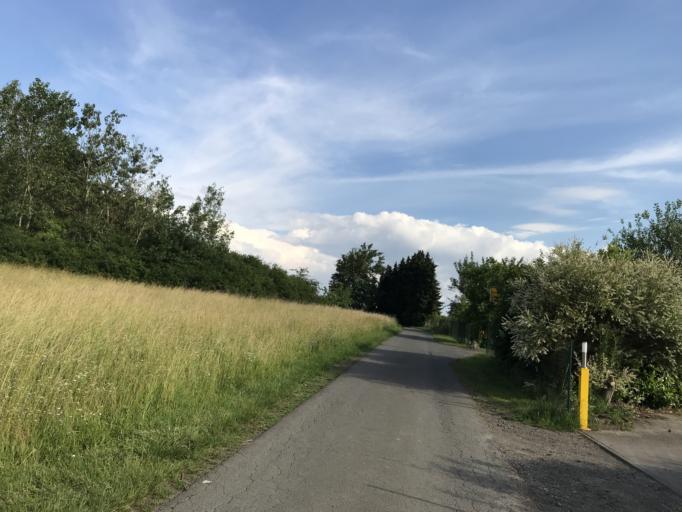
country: DE
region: Hesse
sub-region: Regierungsbezirk Giessen
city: Lich
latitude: 50.5152
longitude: 8.8312
